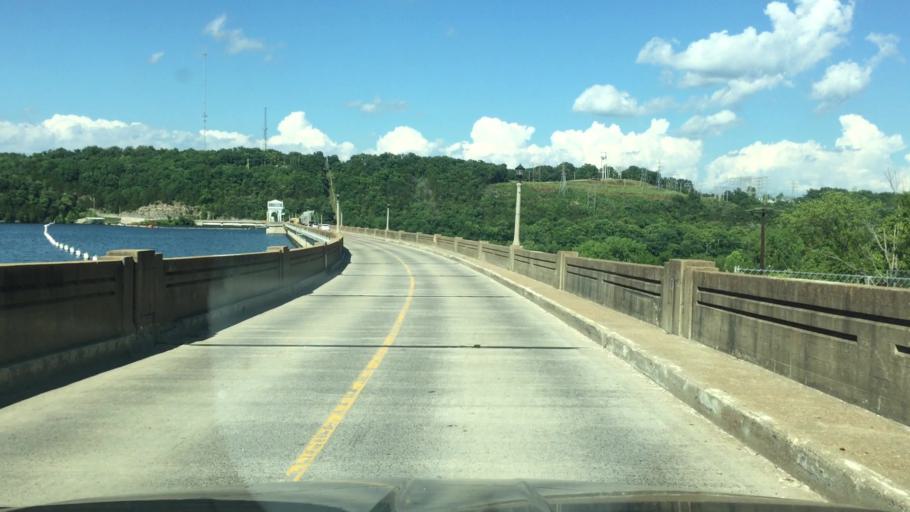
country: US
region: Missouri
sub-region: Miller County
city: Lake Ozark
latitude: 38.2013
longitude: -92.6286
